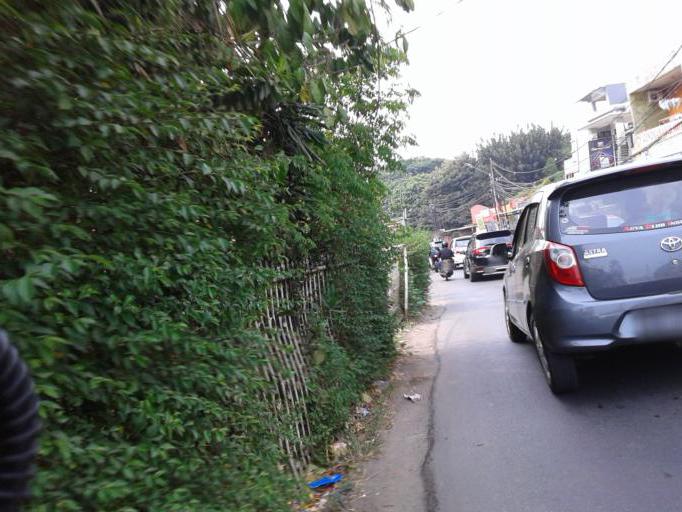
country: ID
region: Banten
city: South Tangerang
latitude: -6.2933
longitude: 106.7330
